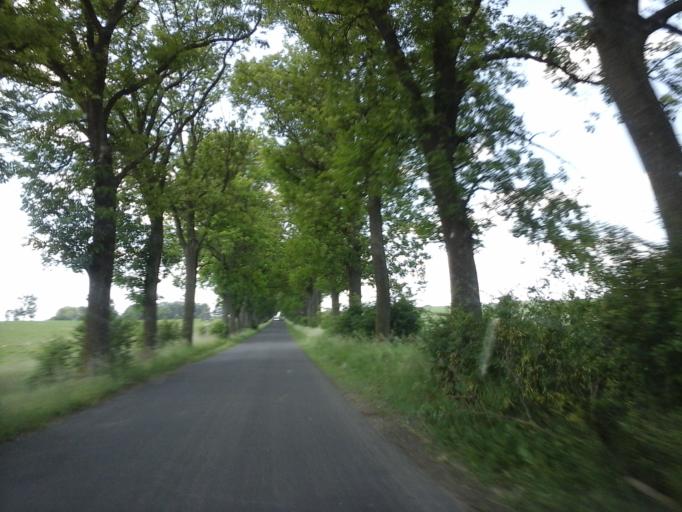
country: PL
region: West Pomeranian Voivodeship
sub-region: Powiat choszczenski
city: Recz
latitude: 53.1800
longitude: 15.6017
